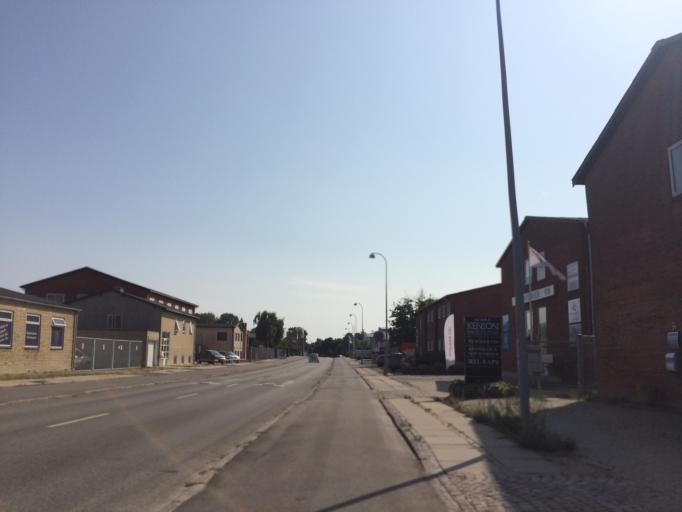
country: DK
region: Capital Region
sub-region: Hvidovre Kommune
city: Hvidovre
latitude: 55.6435
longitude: 12.4712
